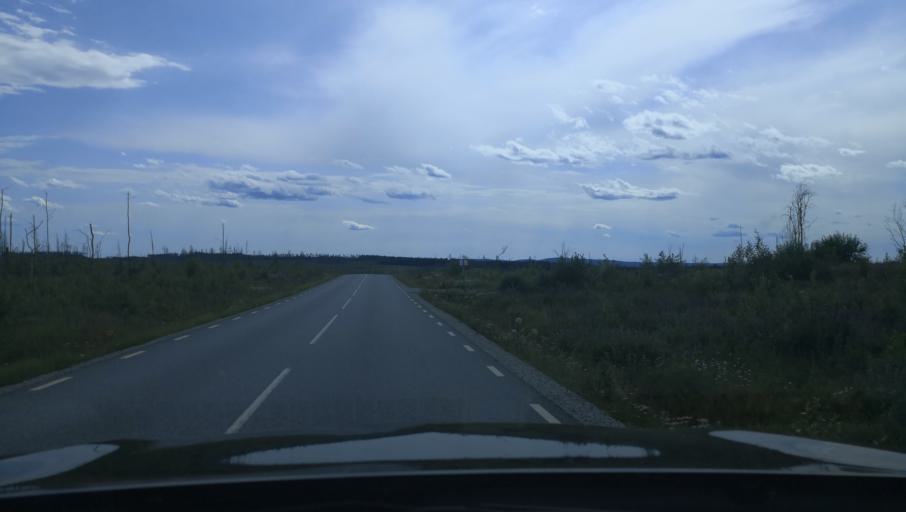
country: SE
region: Vaestmanland
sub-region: Norbergs Kommun
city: Norberg
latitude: 59.9815
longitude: 16.0463
